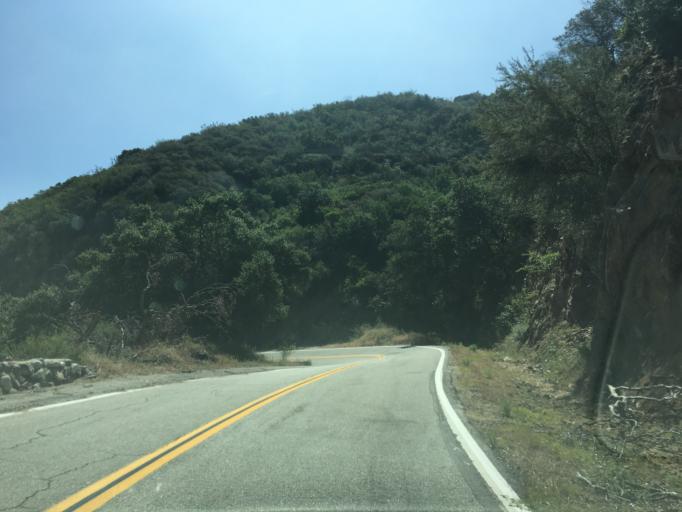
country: US
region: California
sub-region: Los Angeles County
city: Glendora
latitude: 34.2056
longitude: -117.8041
